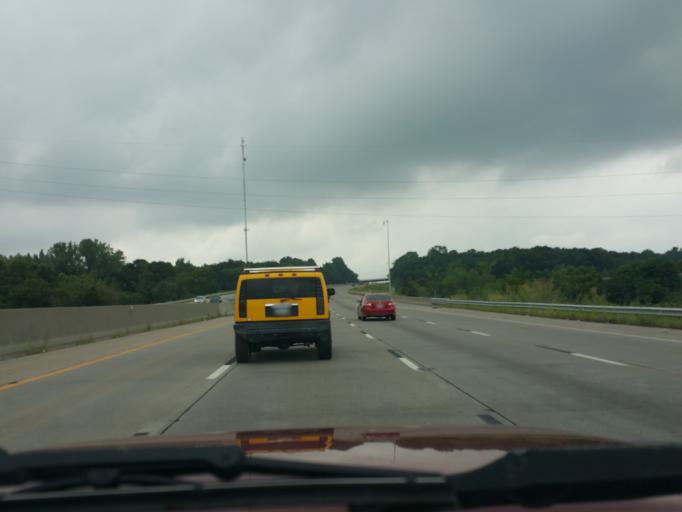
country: US
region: Kansas
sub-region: Johnson County
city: Merriam
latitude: 39.0668
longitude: -94.6798
